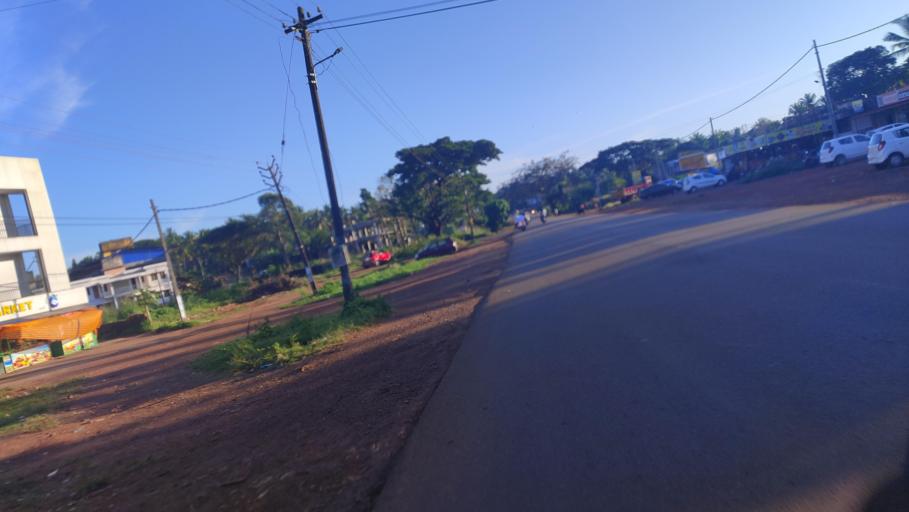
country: IN
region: Kerala
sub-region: Kasaragod District
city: Kasaragod
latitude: 12.4790
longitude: 75.0582
